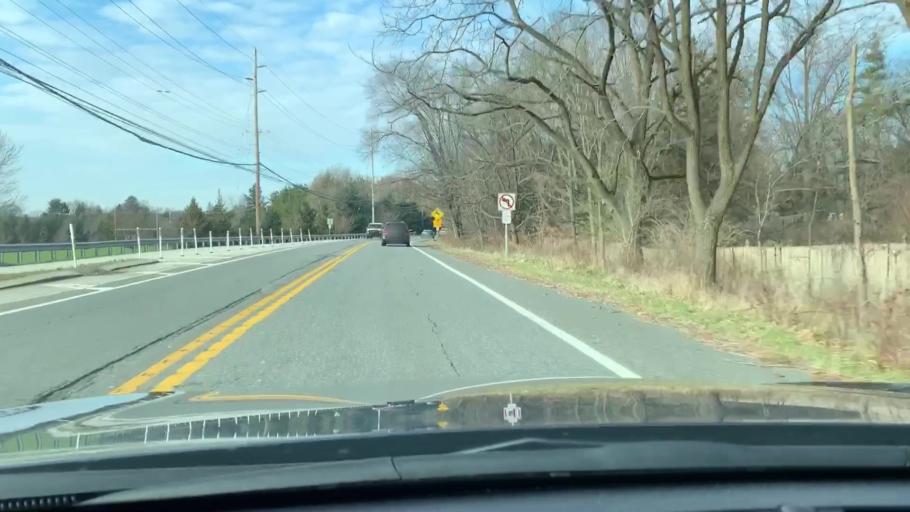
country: US
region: Pennsylvania
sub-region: Chester County
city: Berwyn
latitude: 40.0091
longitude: -75.4260
